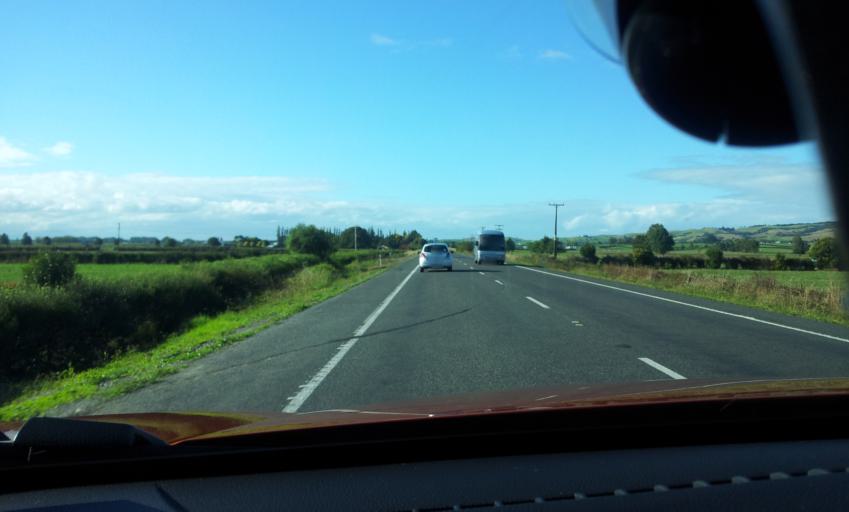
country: NZ
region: Waikato
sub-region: Hauraki District
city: Ngatea
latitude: -37.4111
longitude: 175.4794
